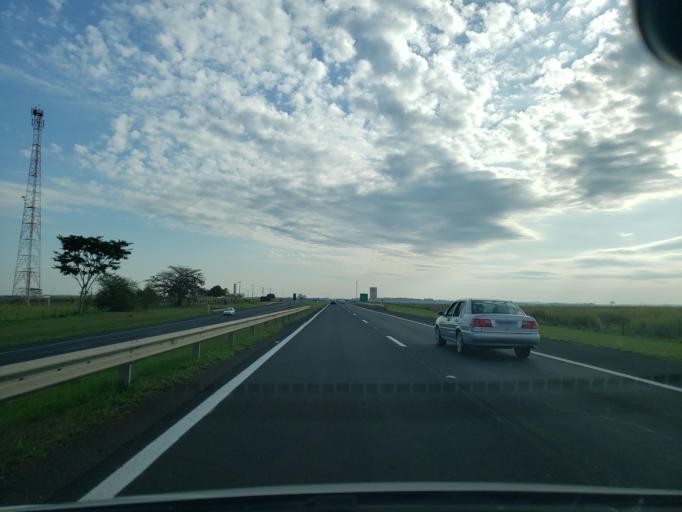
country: BR
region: Sao Paulo
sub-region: Guararapes
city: Guararapes
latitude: -21.2059
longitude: -50.6331
